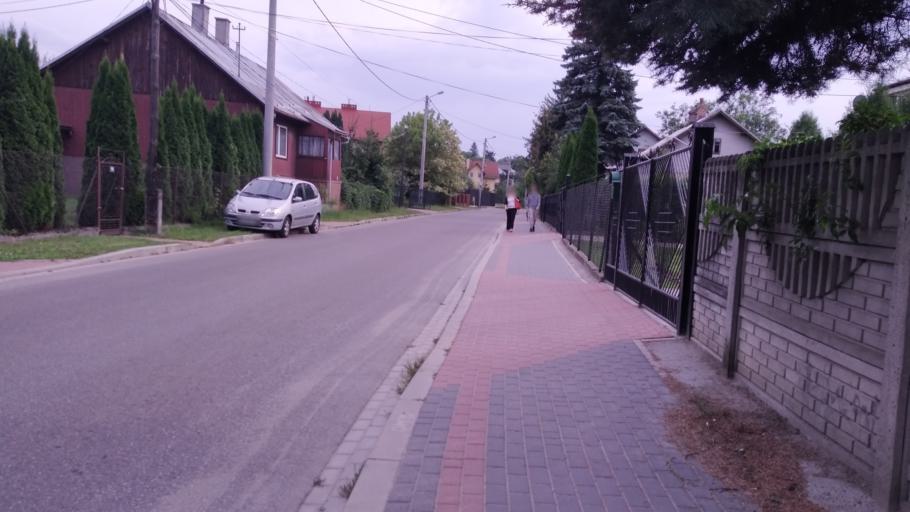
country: PL
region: Subcarpathian Voivodeship
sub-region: Powiat lancucki
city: Lancut
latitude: 50.0767
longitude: 22.2321
